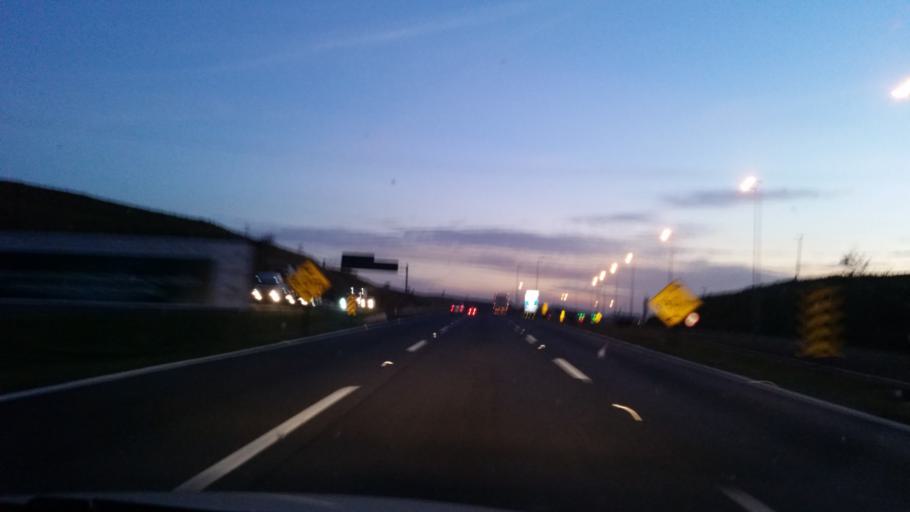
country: BR
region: Sao Paulo
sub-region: Santa Isabel
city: Santa Isabel
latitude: -23.3761
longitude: -46.1424
